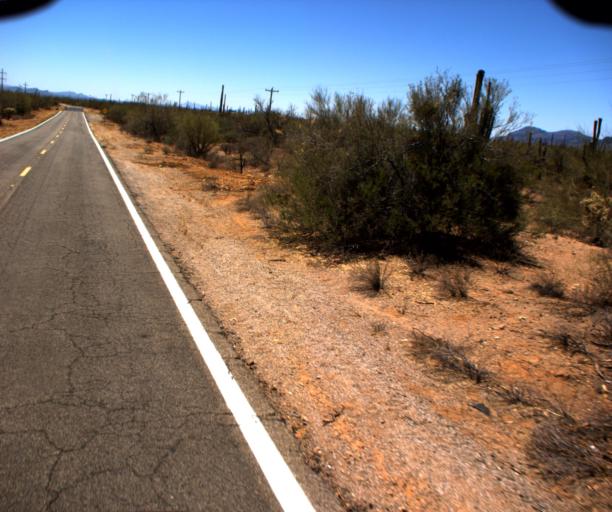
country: US
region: Arizona
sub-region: Pima County
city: Sells
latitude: 32.1456
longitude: -112.1017
